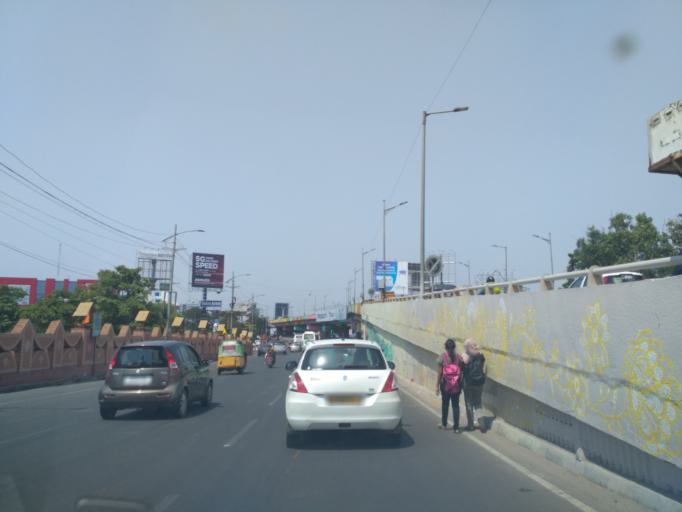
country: IN
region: Telangana
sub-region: Rangareddi
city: Kukatpalli
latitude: 17.4509
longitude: 78.3797
